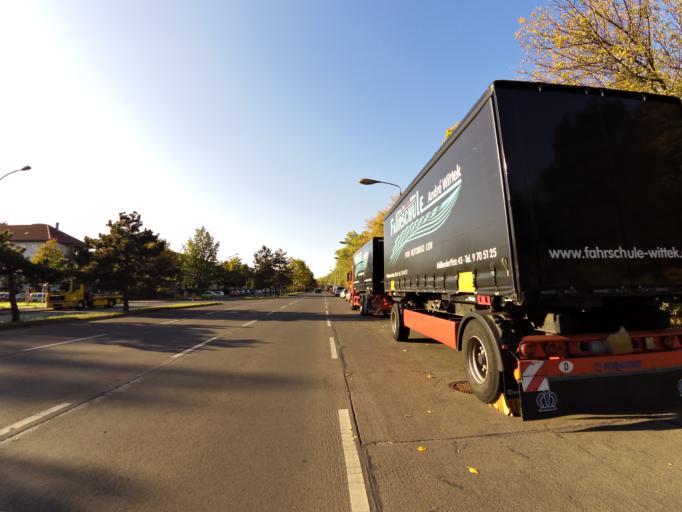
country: DE
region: Berlin
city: Oberschoneweide
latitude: 52.4646
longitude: 13.5263
